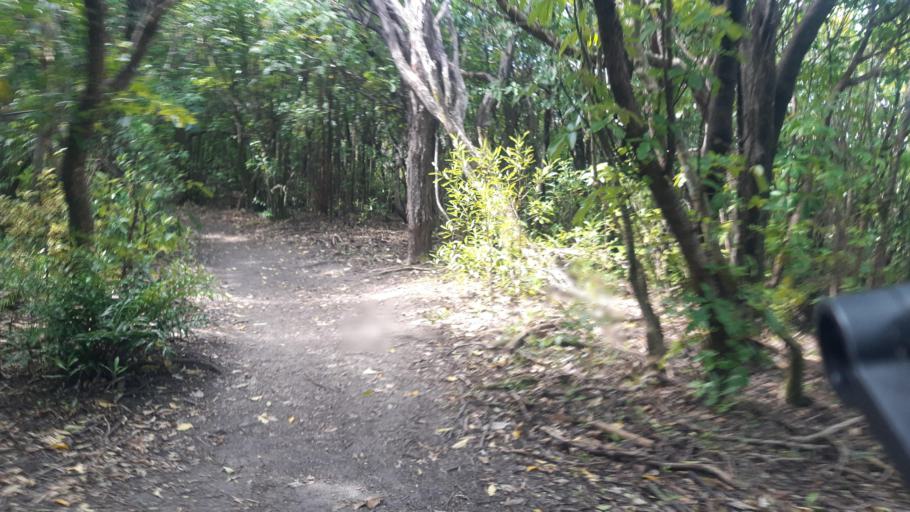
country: NZ
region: Marlborough
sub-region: Marlborough District
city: Picton
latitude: -41.2542
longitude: 174.0436
